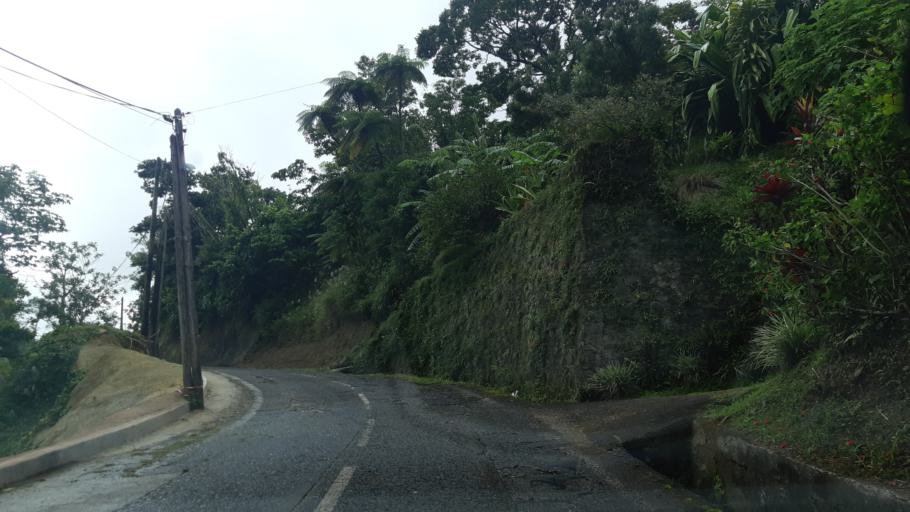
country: GP
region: Guadeloupe
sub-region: Guadeloupe
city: Saint-Claude
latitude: 16.0460
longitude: -61.6914
